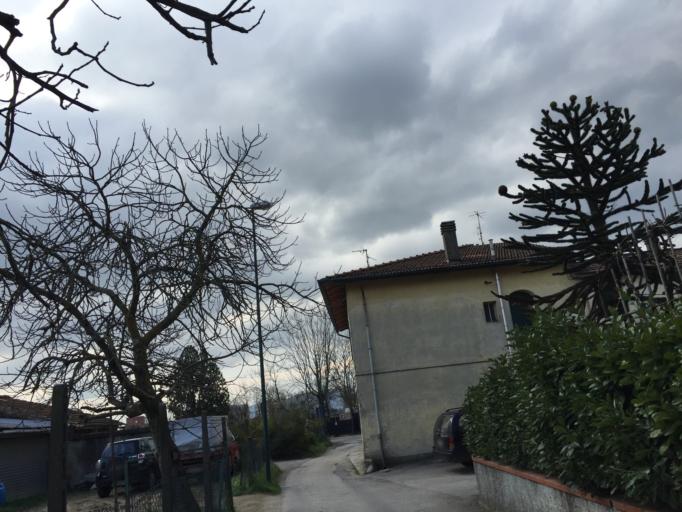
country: IT
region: Tuscany
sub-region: Provincia di Prato
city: Fornacelle
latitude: 43.8940
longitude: 11.0558
